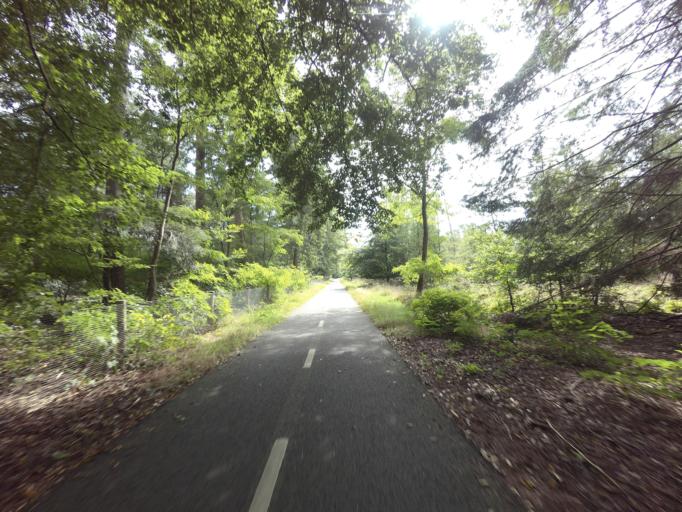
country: NL
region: Drenthe
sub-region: Gemeente Borger-Odoorn
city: Borger
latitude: 52.8831
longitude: 6.7173
